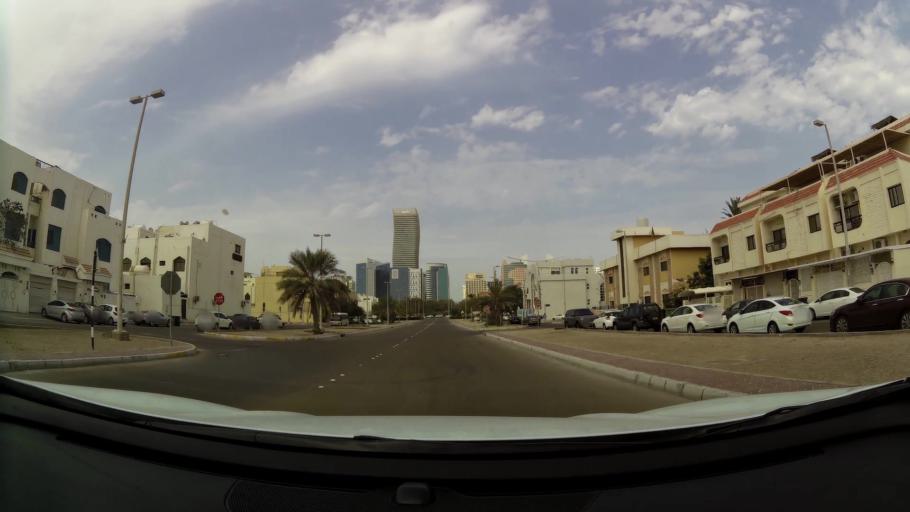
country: AE
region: Abu Dhabi
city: Abu Dhabi
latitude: 24.4635
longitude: 54.3456
